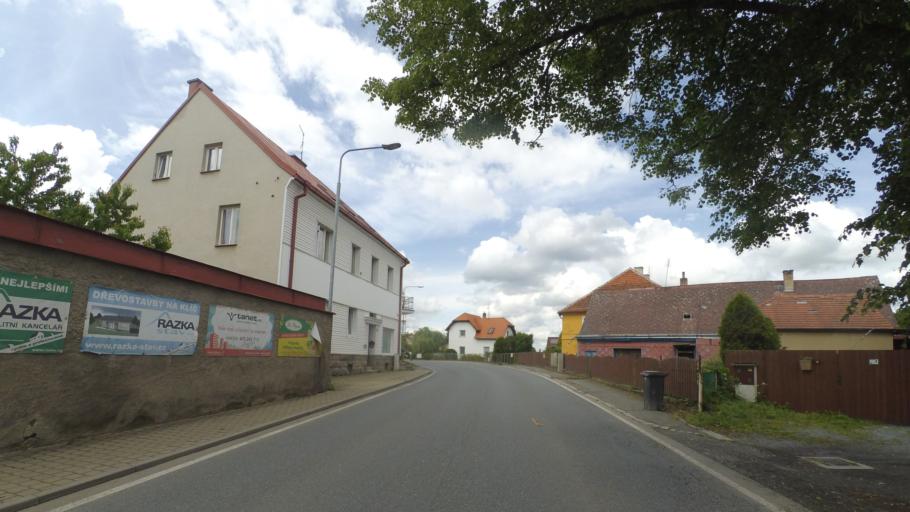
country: CZ
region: Plzensky
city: Bor
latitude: 49.7122
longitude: 12.7774
